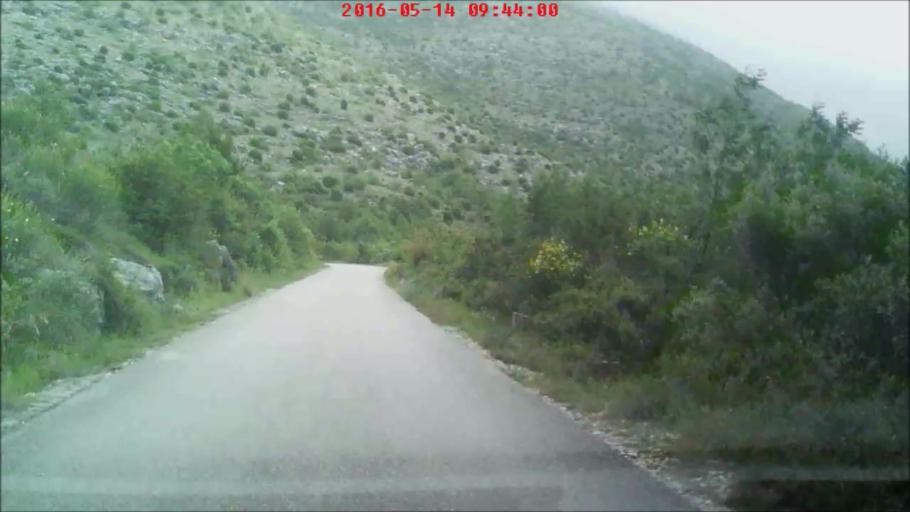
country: HR
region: Dubrovacko-Neretvanska
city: Podgora
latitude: 42.7855
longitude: 17.9068
